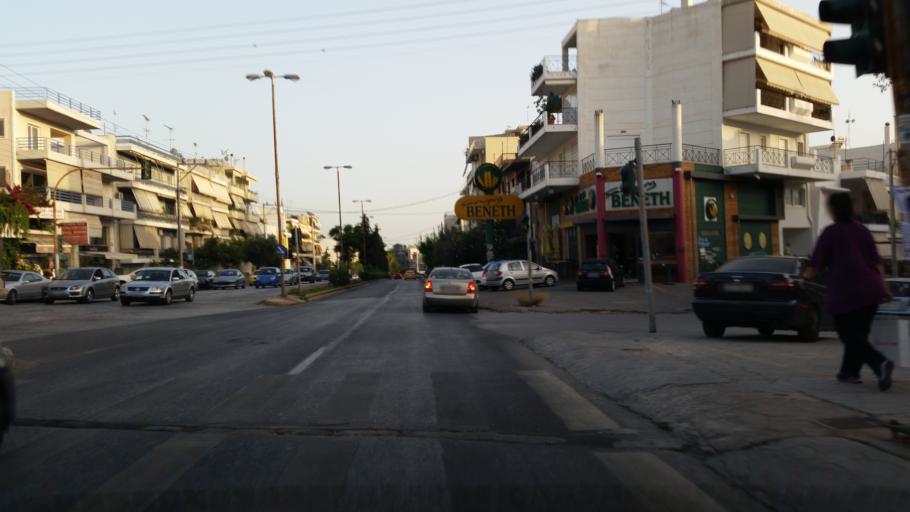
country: GR
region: Attica
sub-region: Nomarchia Athinas
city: Argyroupoli
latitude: 37.9082
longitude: 23.7541
